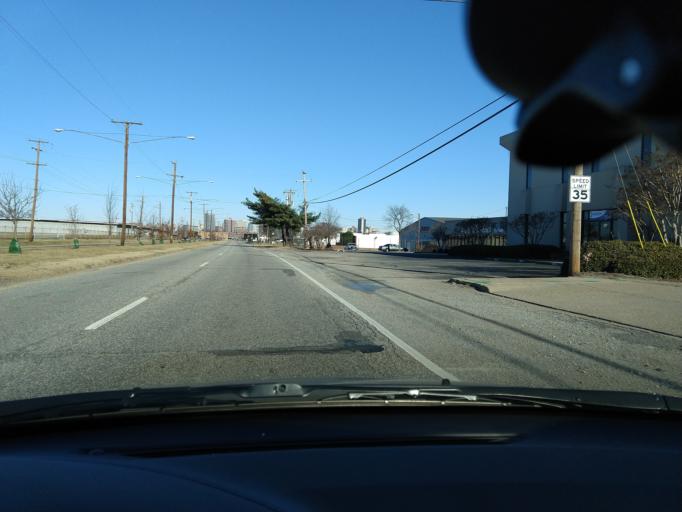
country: US
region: Virginia
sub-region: City of Richmond
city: Richmond
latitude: 37.5087
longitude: -77.4310
